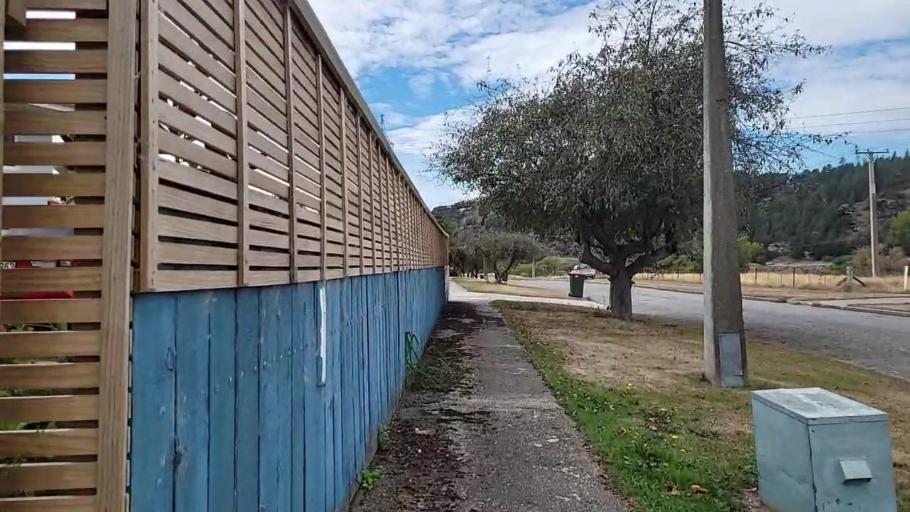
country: NZ
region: Otago
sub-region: Queenstown-Lakes District
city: Kingston
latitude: -45.4805
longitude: 169.3144
